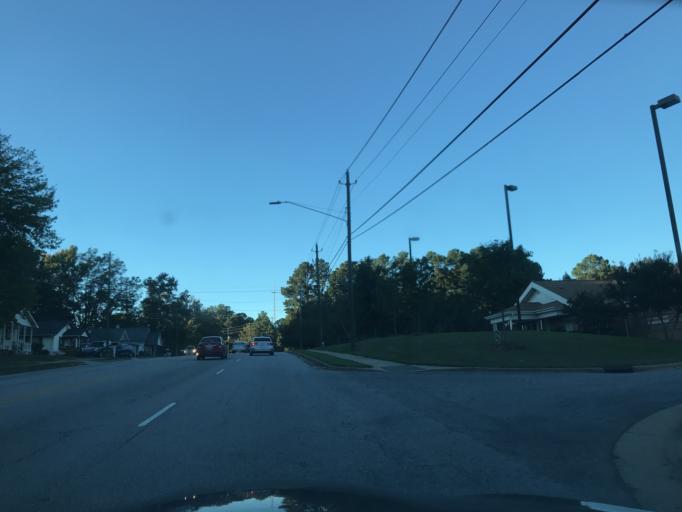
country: US
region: North Carolina
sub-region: Wake County
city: Raleigh
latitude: 35.7666
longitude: -78.6159
